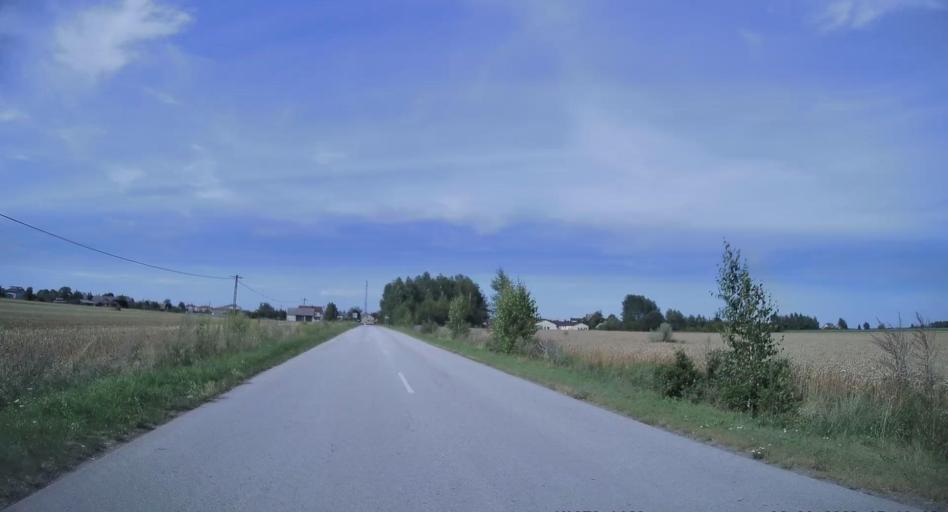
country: PL
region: Lodz Voivodeship
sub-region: Powiat opoczynski
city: Mniszkow
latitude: 51.3667
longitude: 20.0386
